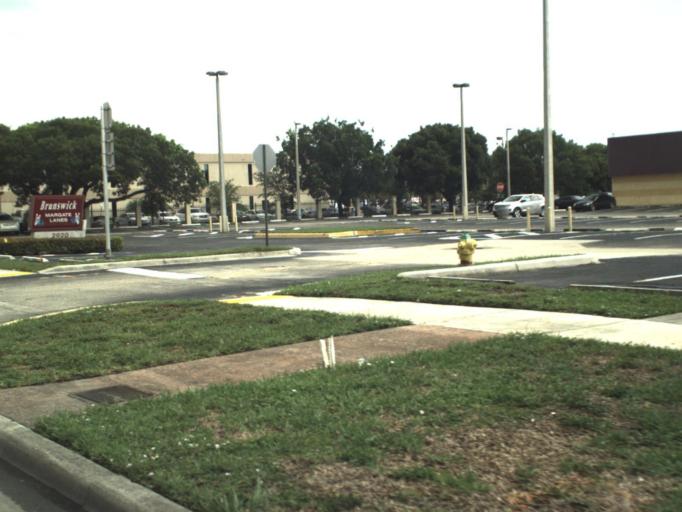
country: US
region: Florida
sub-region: Broward County
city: Margate
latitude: 26.2528
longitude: -80.2014
